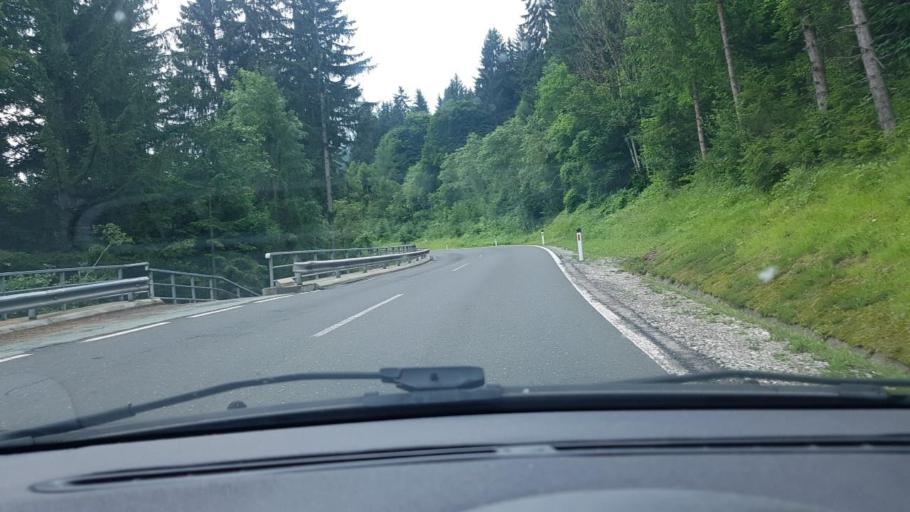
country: AT
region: Carinthia
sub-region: Politischer Bezirk Spittal an der Drau
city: Greifenburg
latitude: 46.7349
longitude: 13.2220
